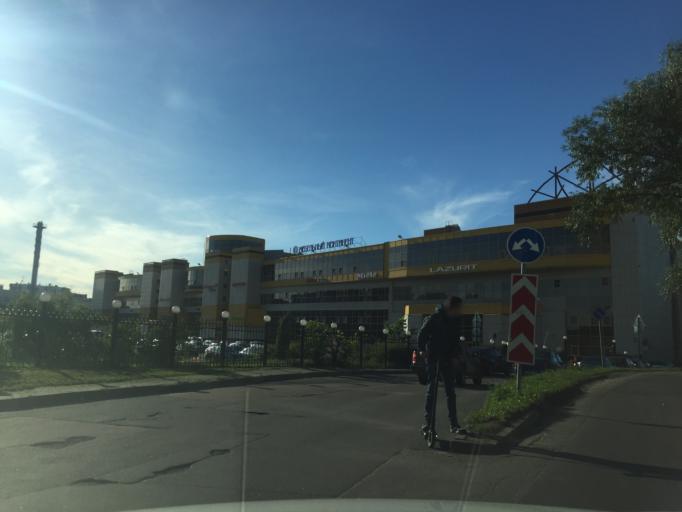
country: RU
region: St.-Petersburg
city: Admiralteisky
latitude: 59.8805
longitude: 30.3128
